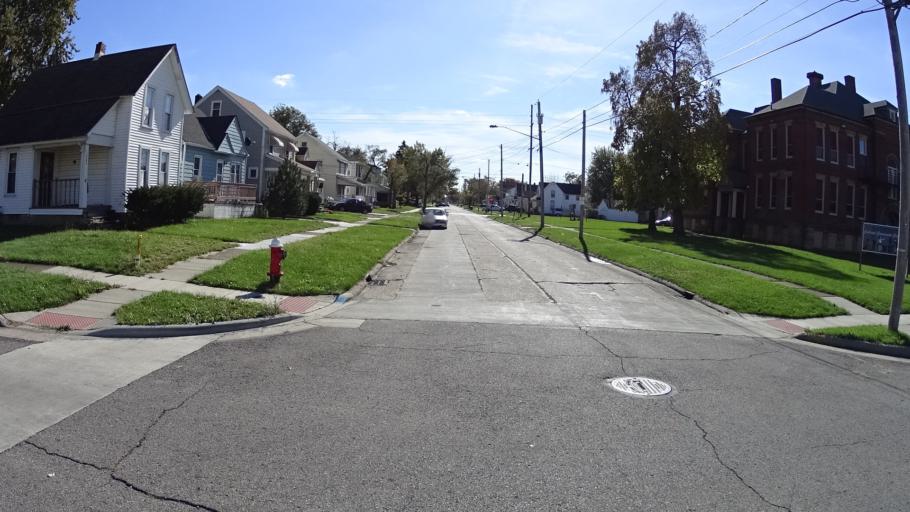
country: US
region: Ohio
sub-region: Lorain County
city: Lorain
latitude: 41.4527
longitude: -82.1822
